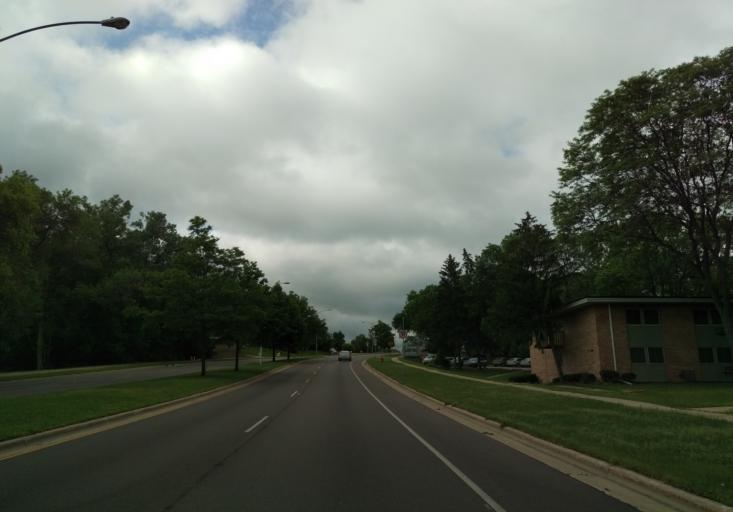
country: US
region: Wisconsin
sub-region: Dane County
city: Middleton
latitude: 43.0927
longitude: -89.4858
